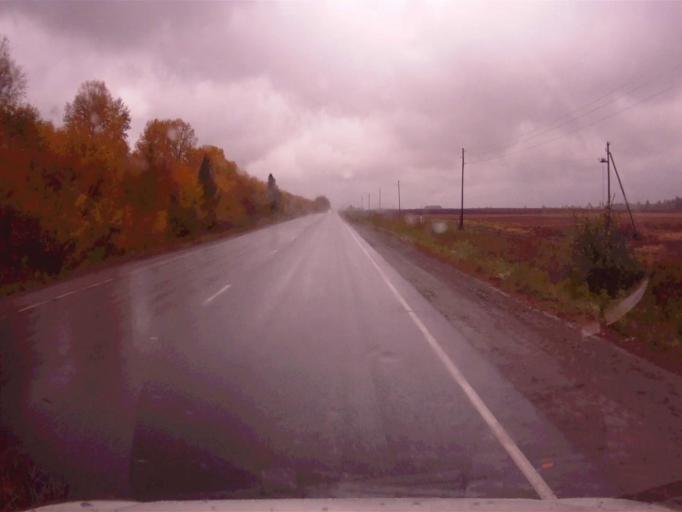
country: RU
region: Chelyabinsk
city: Argayash
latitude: 55.4253
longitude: 61.0041
